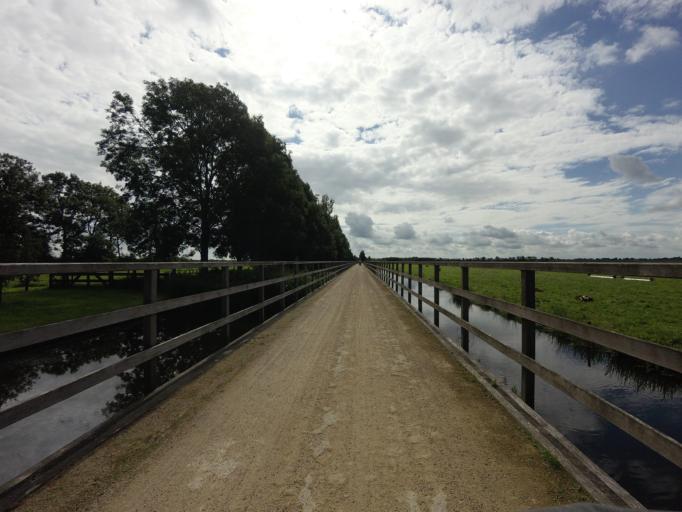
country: NL
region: South Holland
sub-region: Gemeente Vlist
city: Vlist
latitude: 51.9988
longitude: 4.8193
